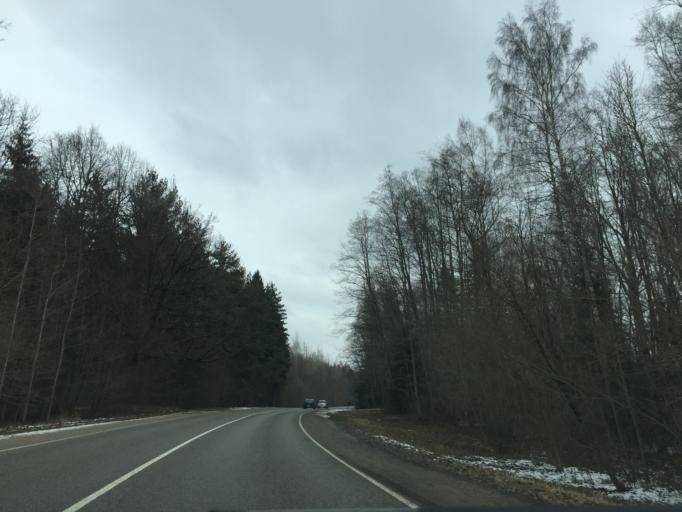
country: LV
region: Kegums
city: Kegums
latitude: 56.7539
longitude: 24.7351
